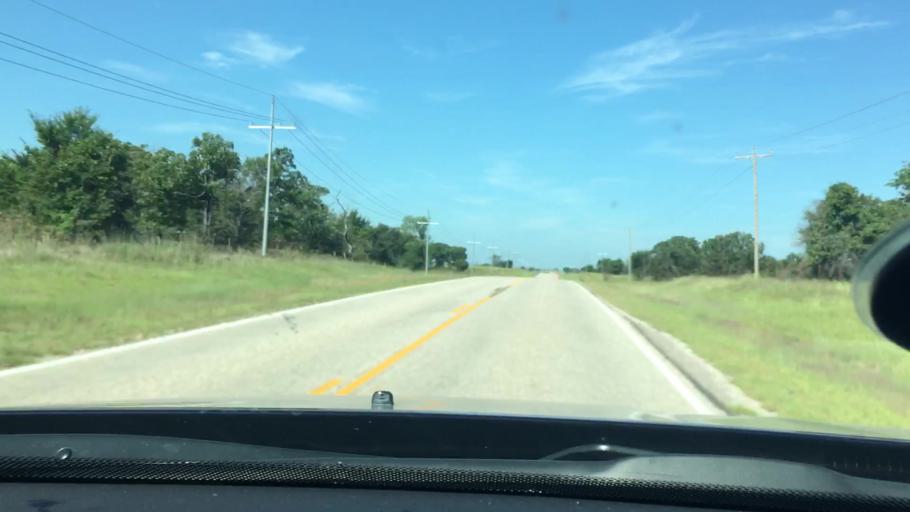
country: US
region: Oklahoma
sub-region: Johnston County
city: Tishomingo
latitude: 34.3613
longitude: -96.6067
